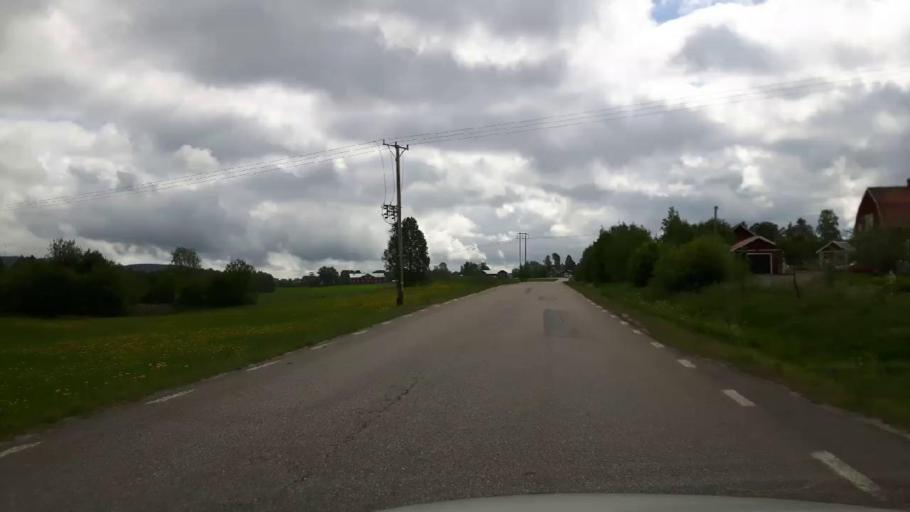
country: SE
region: Gaevleborg
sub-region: Ovanakers Kommun
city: Edsbyn
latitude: 61.3574
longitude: 15.9004
